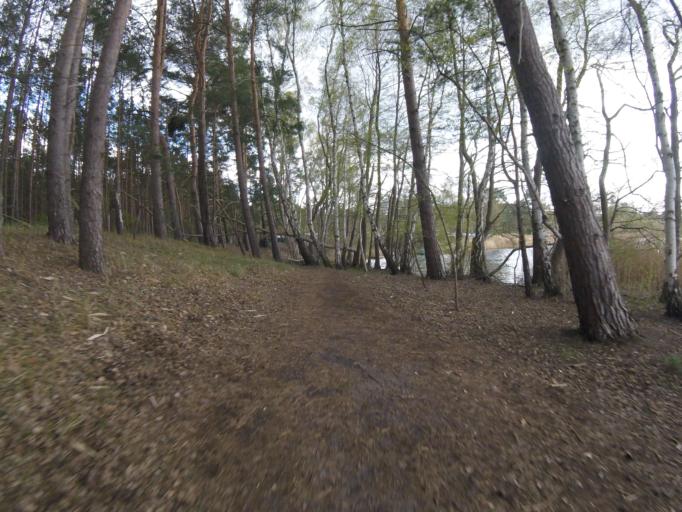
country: DE
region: Brandenburg
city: Bestensee
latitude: 52.2579
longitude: 13.6717
